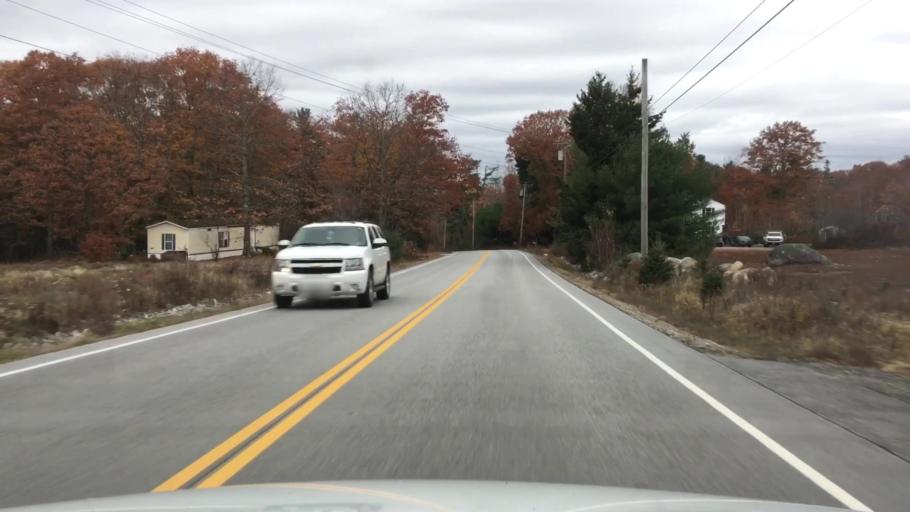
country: US
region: Maine
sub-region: Hancock County
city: Orland
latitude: 44.5538
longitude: -68.6943
